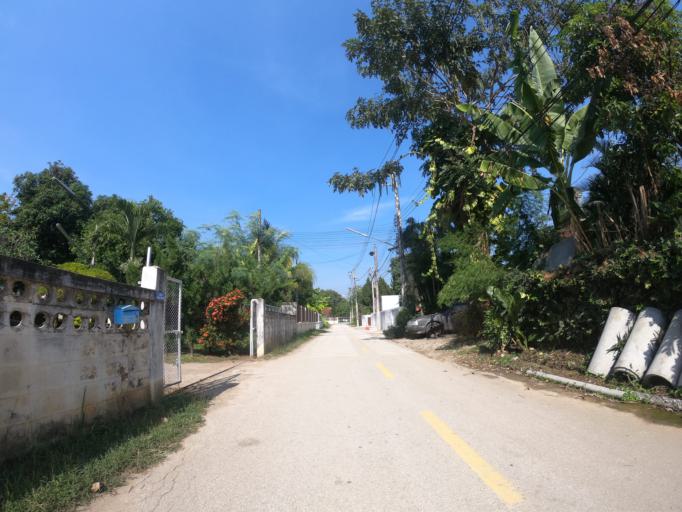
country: TH
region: Chiang Mai
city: Chiang Mai
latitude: 18.7720
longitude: 99.0040
